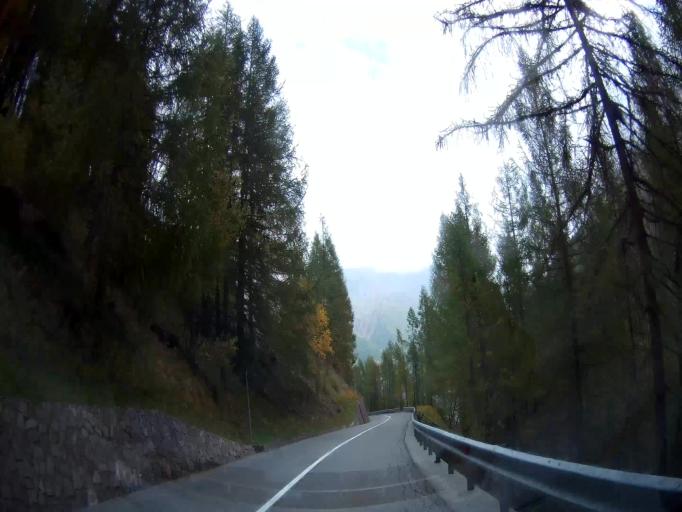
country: IT
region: Trentino-Alto Adige
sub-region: Bolzano
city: Senales
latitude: 46.7343
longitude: 10.8154
